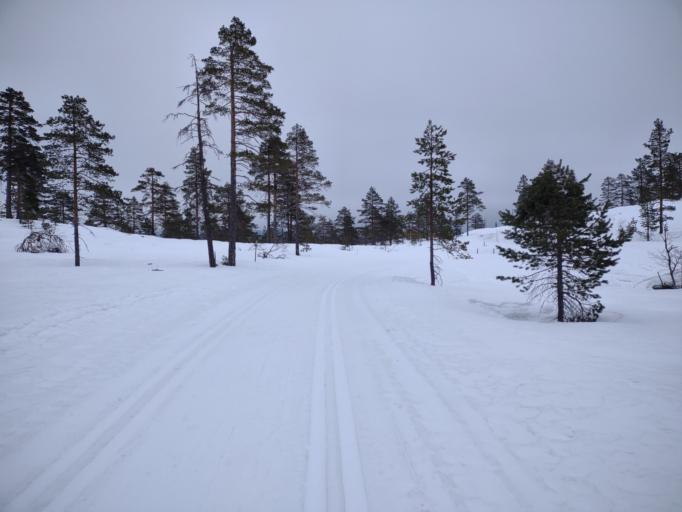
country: NO
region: Buskerud
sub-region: Flesberg
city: Lampeland
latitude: 59.7937
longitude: 9.4401
